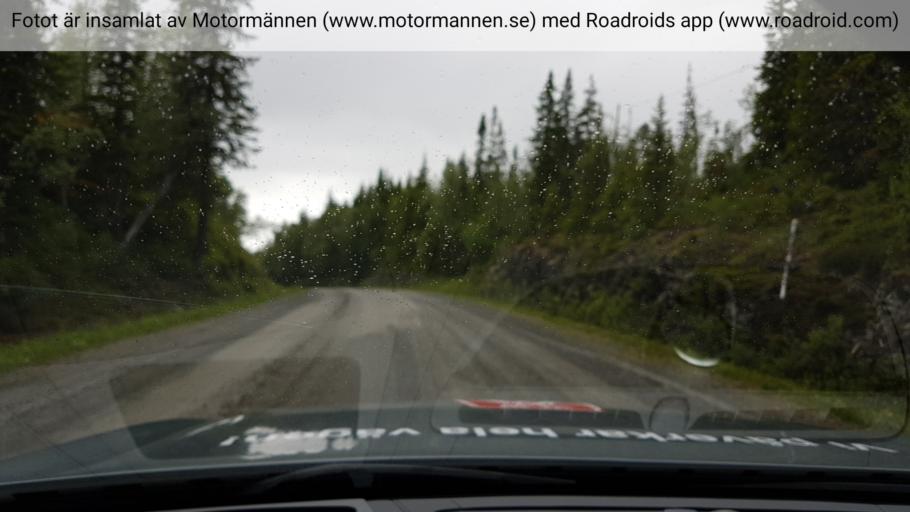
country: NO
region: Nord-Trondelag
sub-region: Snasa
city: Snaase
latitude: 63.7287
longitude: 12.5740
